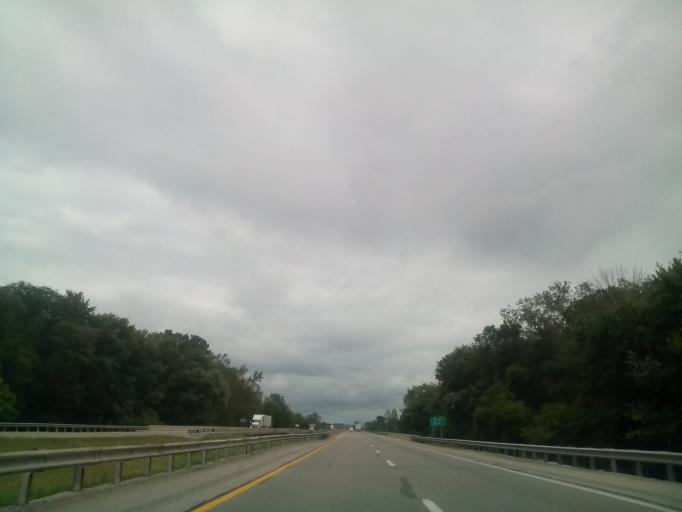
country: US
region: Ohio
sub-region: Fulton County
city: Burlington
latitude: 41.5877
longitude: -84.3389
